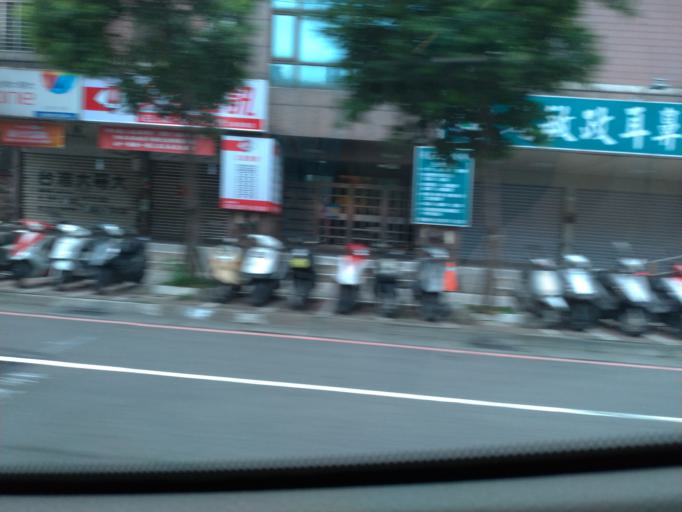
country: TW
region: Taiwan
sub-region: Taoyuan
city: Taoyuan
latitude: 24.9377
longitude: 121.3723
